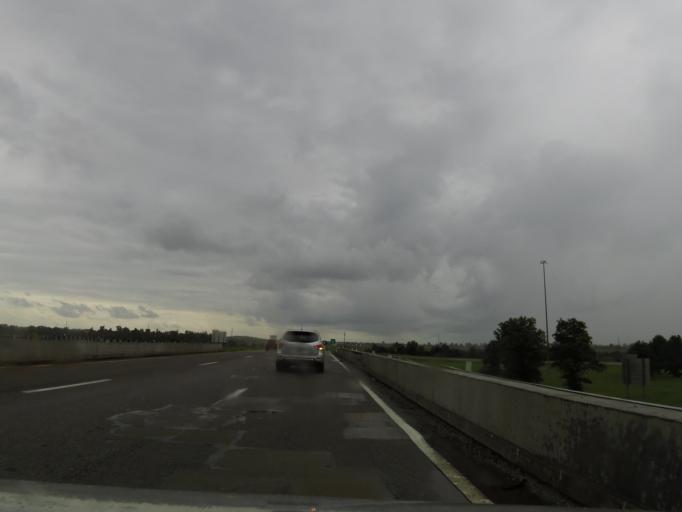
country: US
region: Missouri
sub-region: Scott County
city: Sikeston
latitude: 36.8737
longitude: -89.5334
